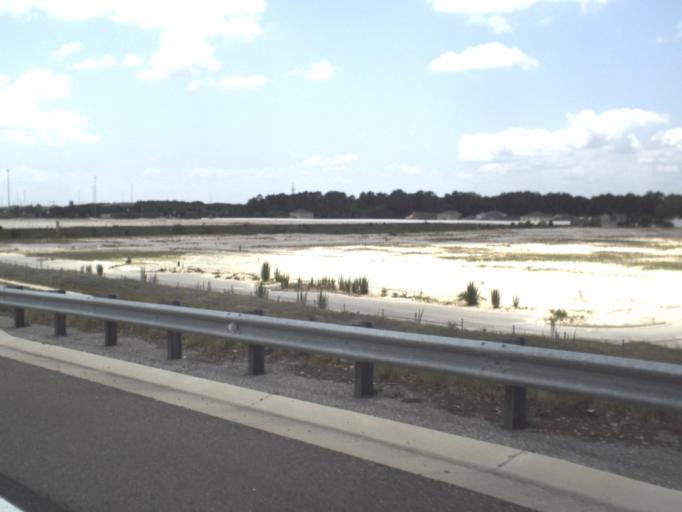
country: US
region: Florida
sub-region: Duval County
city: Jacksonville
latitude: 30.3370
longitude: -81.5524
